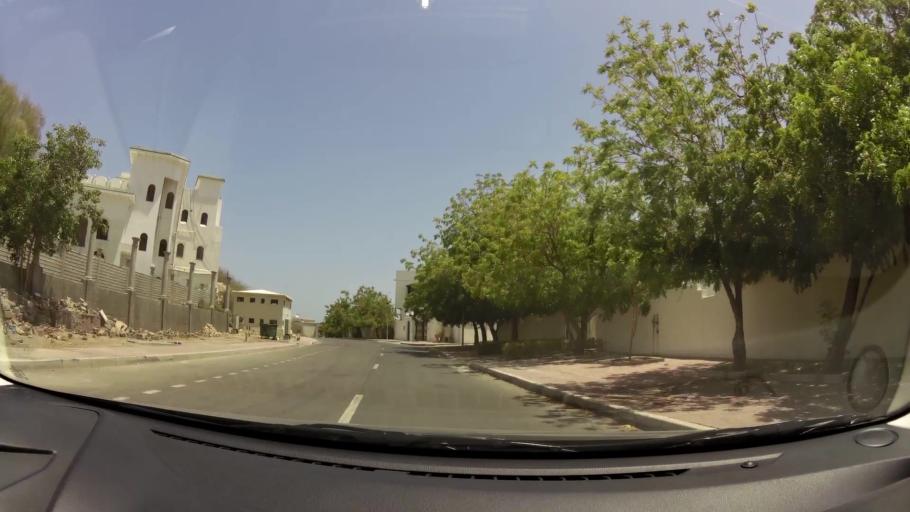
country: OM
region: Muhafazat Masqat
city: Bawshar
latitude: 23.6079
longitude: 58.4754
